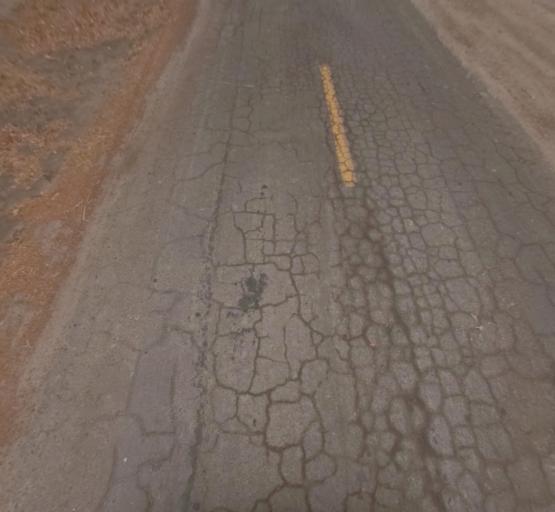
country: US
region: California
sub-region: Madera County
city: Madera
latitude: 36.9113
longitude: -120.1558
